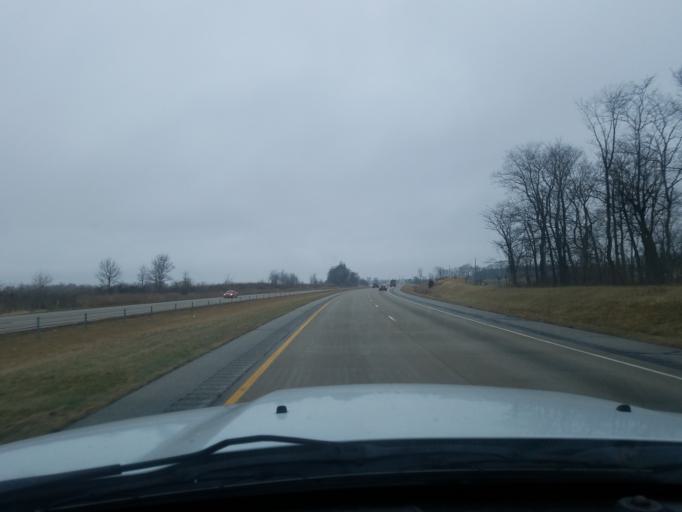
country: US
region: Indiana
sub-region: Grant County
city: Upland
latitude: 40.4607
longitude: -85.5514
